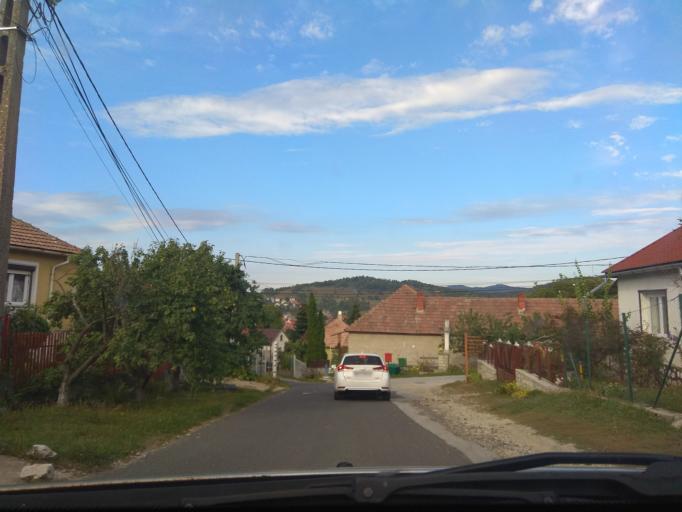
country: HU
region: Borsod-Abauj-Zemplen
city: Saly
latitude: 48.0689
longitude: 20.6411
